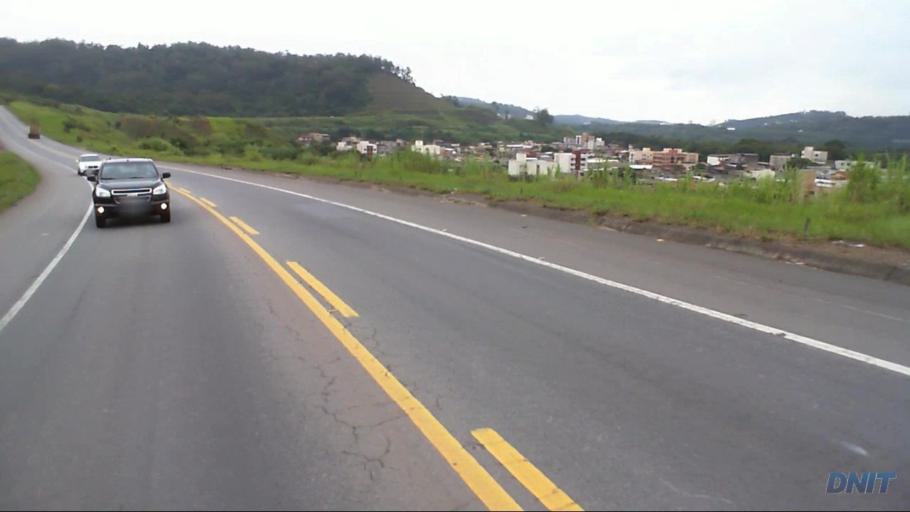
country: BR
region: Minas Gerais
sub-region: Coronel Fabriciano
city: Coronel Fabriciano
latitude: -19.5279
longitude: -42.5798
